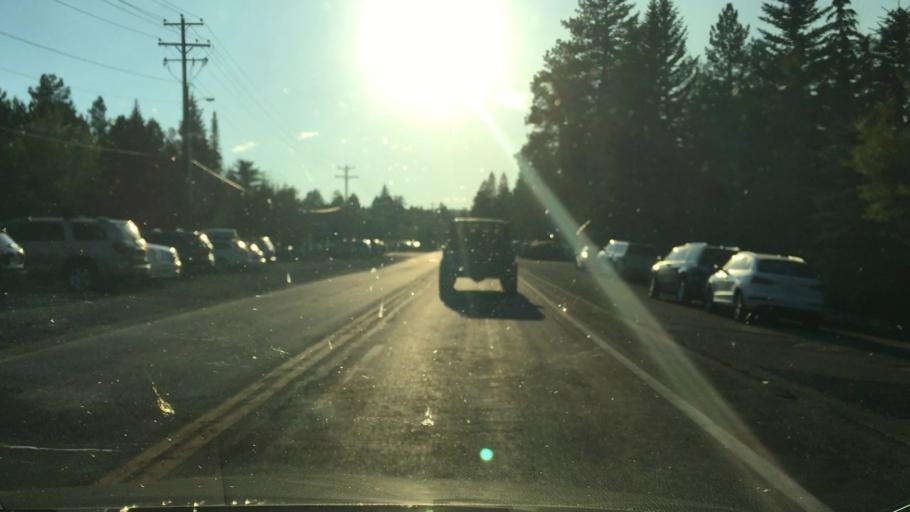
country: US
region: Idaho
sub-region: Valley County
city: McCall
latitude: 44.9121
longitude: -116.1195
